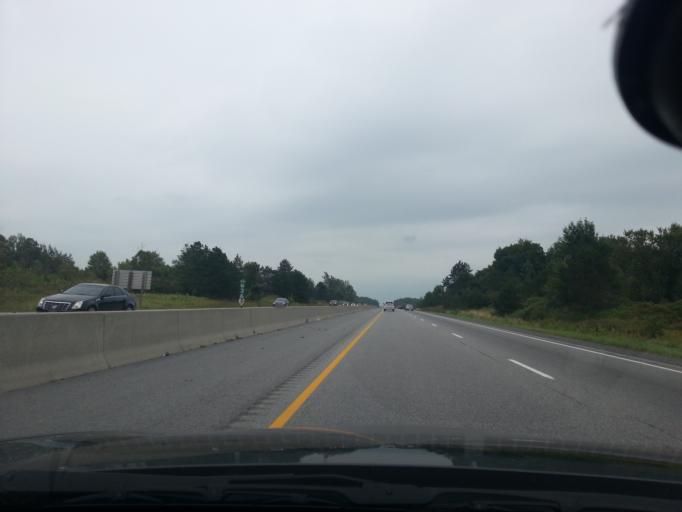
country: CA
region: Ontario
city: Gananoque
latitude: 44.3269
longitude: -76.2810
